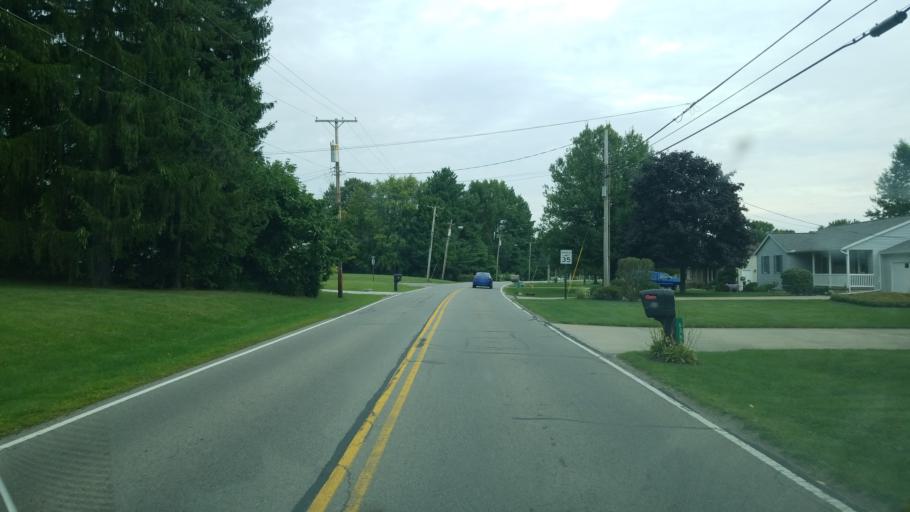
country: US
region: Ohio
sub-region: Richland County
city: Ontario
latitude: 40.7691
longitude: -82.6474
